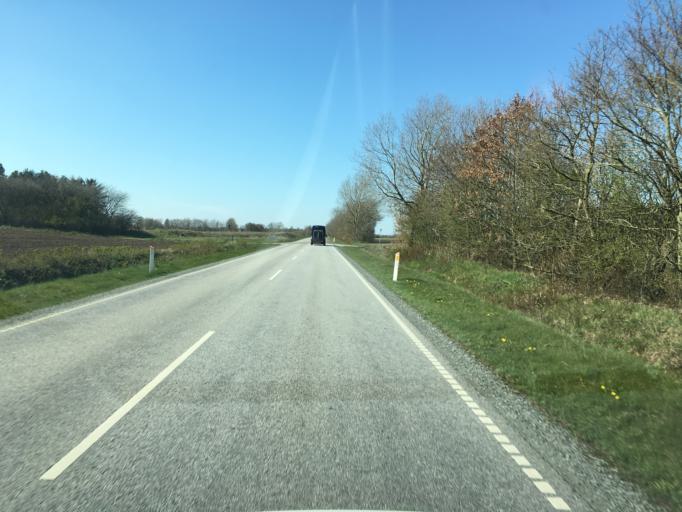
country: DK
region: South Denmark
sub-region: Aabenraa Kommune
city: Tinglev
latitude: 54.9542
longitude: 9.3394
